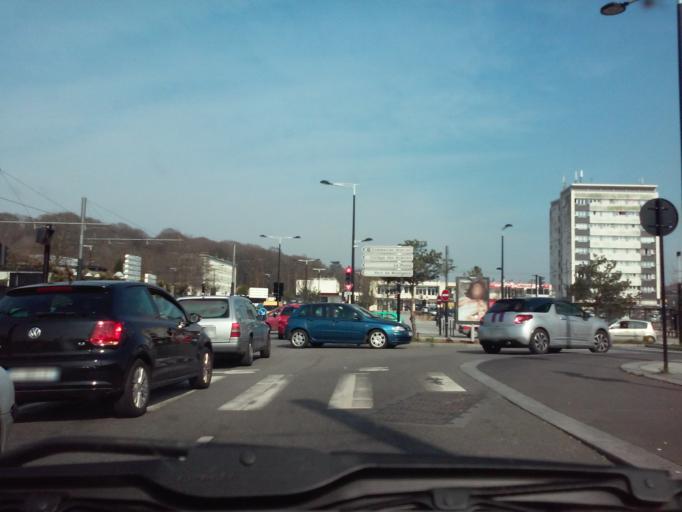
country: FR
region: Haute-Normandie
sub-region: Departement de la Seine-Maritime
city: Fontaine-la-Mallet
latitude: 49.5088
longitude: 0.1356
